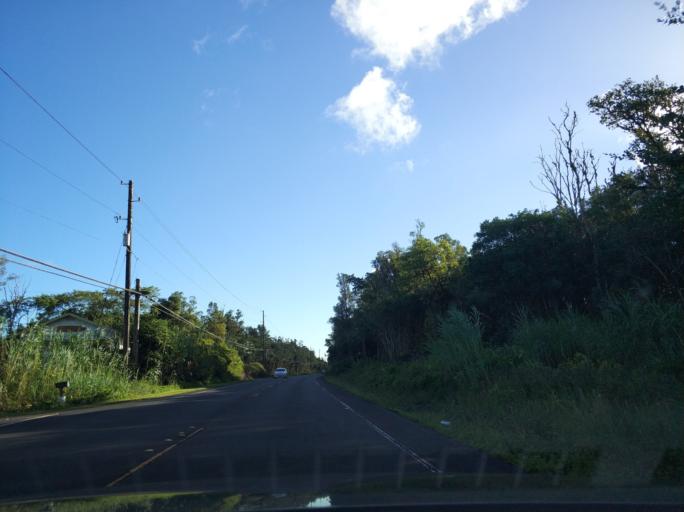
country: US
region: Hawaii
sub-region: Hawaii County
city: Leilani Estates
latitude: 19.4467
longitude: -154.9416
